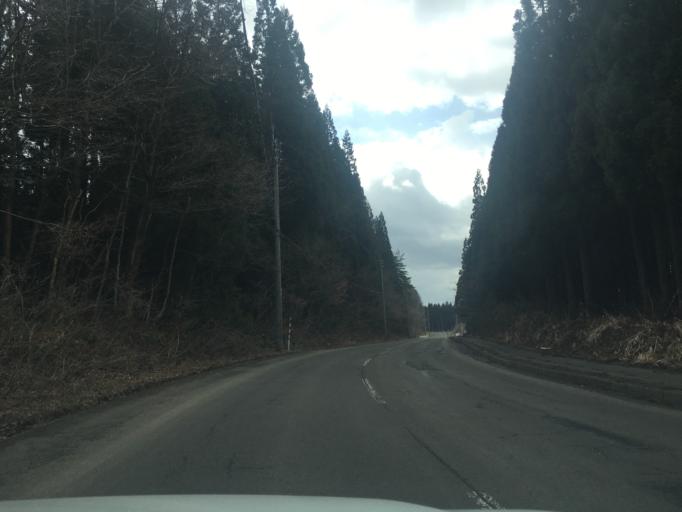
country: JP
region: Akita
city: Takanosu
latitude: 40.1851
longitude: 140.3537
